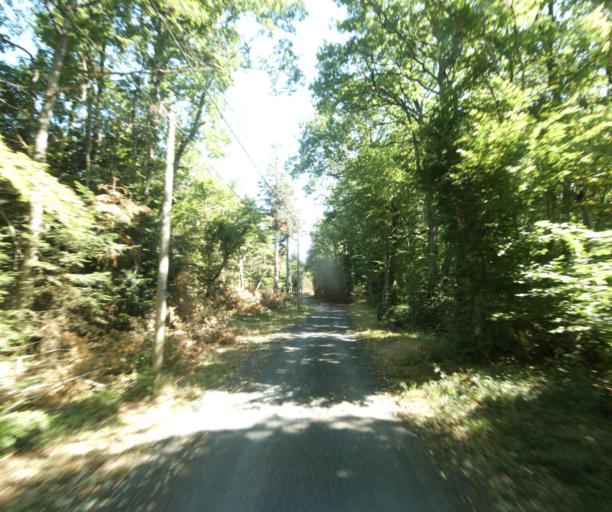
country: FR
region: Rhone-Alpes
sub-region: Departement du Rhone
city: Saint-Romain-de-Popey
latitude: 45.8199
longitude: 4.5160
